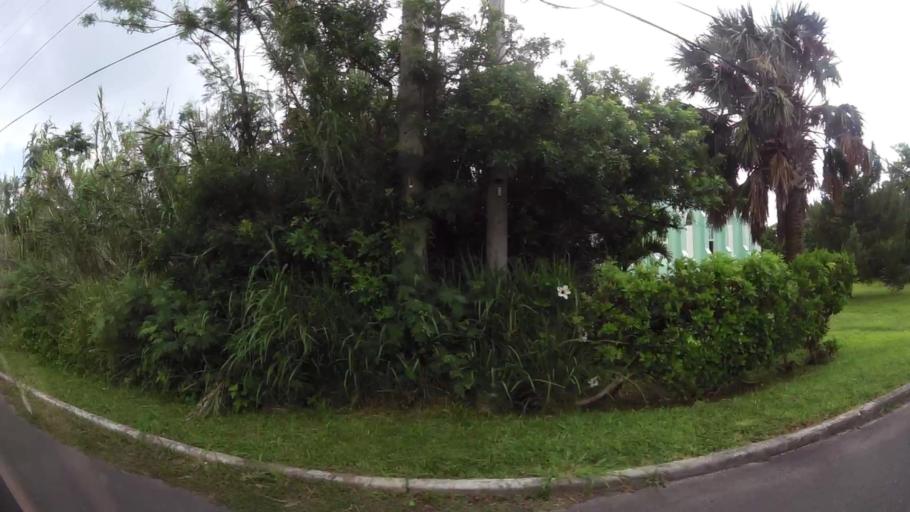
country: BM
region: Saint George
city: Saint George
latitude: 32.3844
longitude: -64.6740
